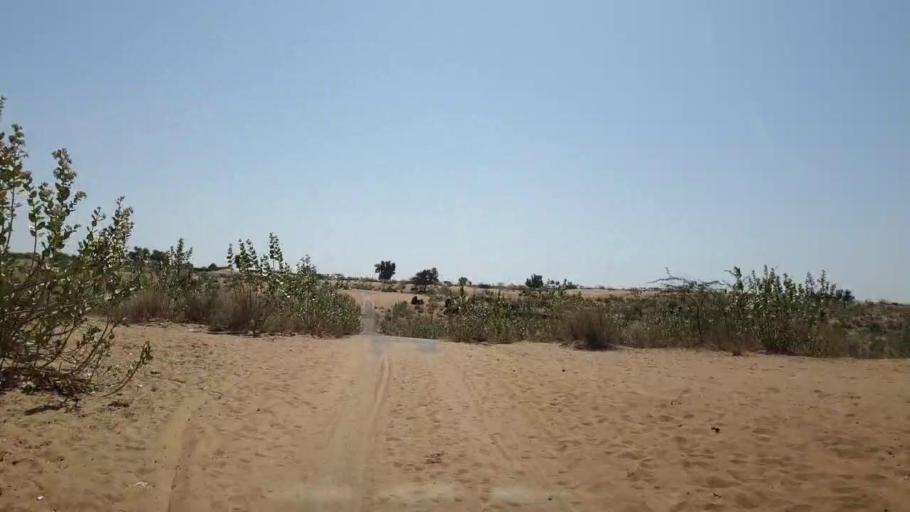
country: PK
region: Sindh
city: Nabisar
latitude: 25.0770
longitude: 69.9828
